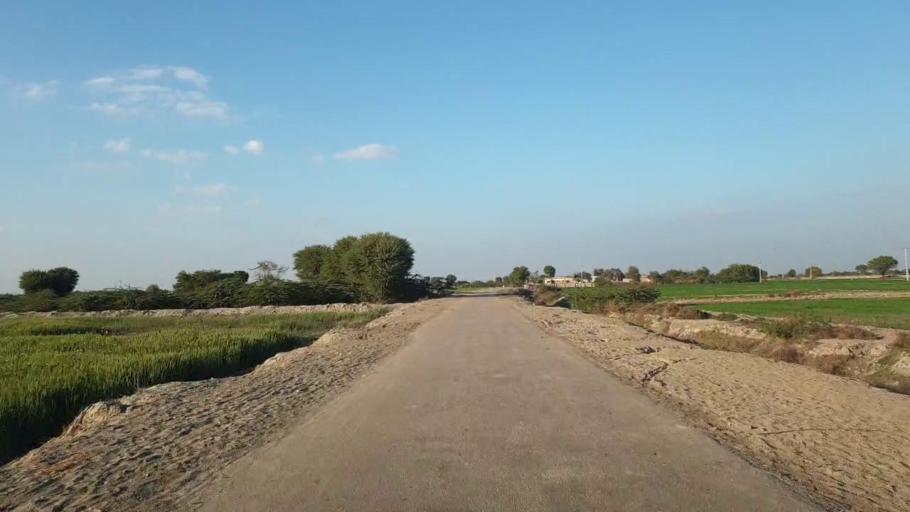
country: PK
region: Sindh
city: Shahpur Chakar
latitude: 26.1460
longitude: 68.5461
